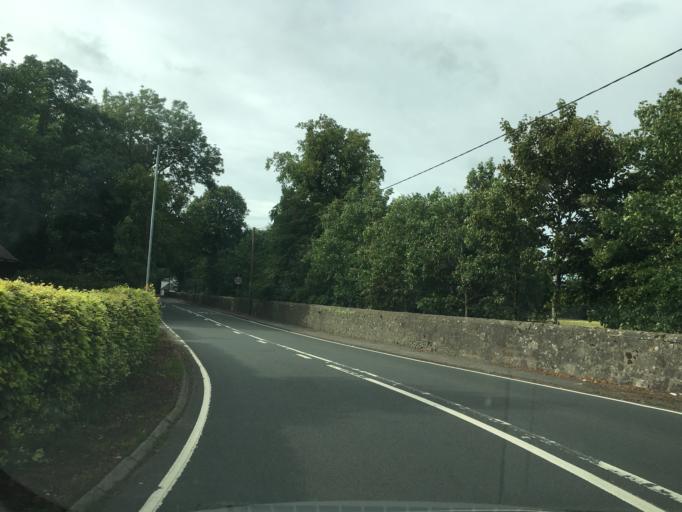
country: GB
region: Scotland
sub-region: South Lanarkshire
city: Biggar
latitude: 55.5898
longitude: -3.5500
